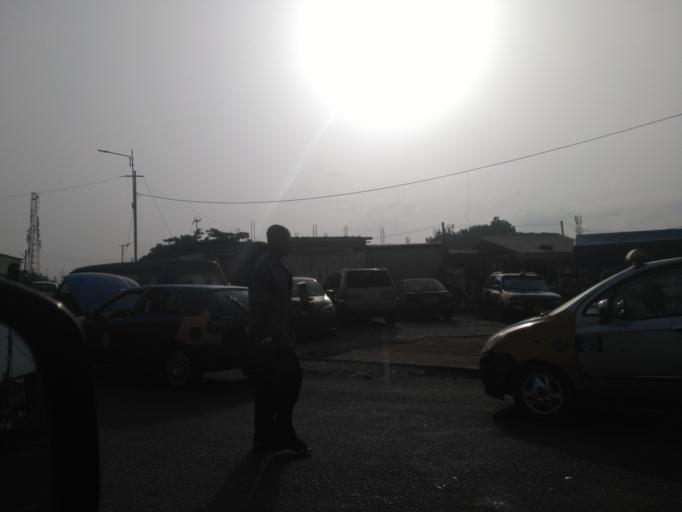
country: GH
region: Greater Accra
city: Accra
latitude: 5.5778
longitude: -0.2007
